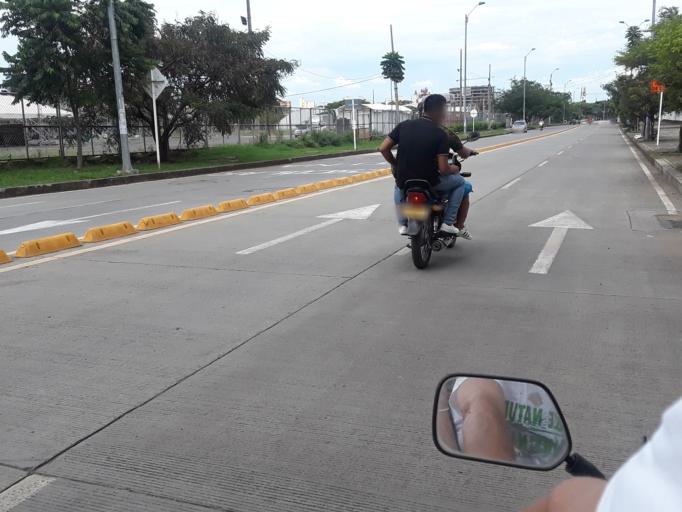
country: CO
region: Valle del Cauca
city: Cali
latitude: 3.4173
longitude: -76.5528
